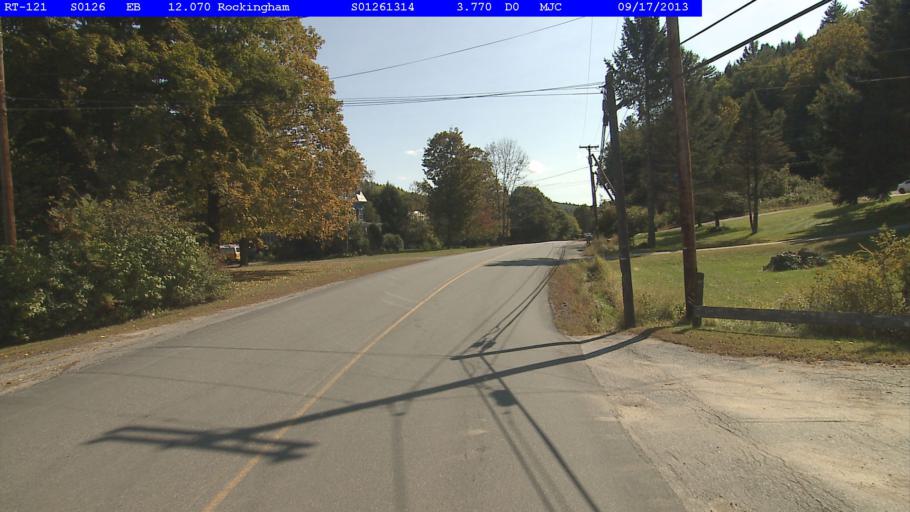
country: US
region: Vermont
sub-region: Windham County
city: Rockingham
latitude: 43.1410
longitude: -72.4948
